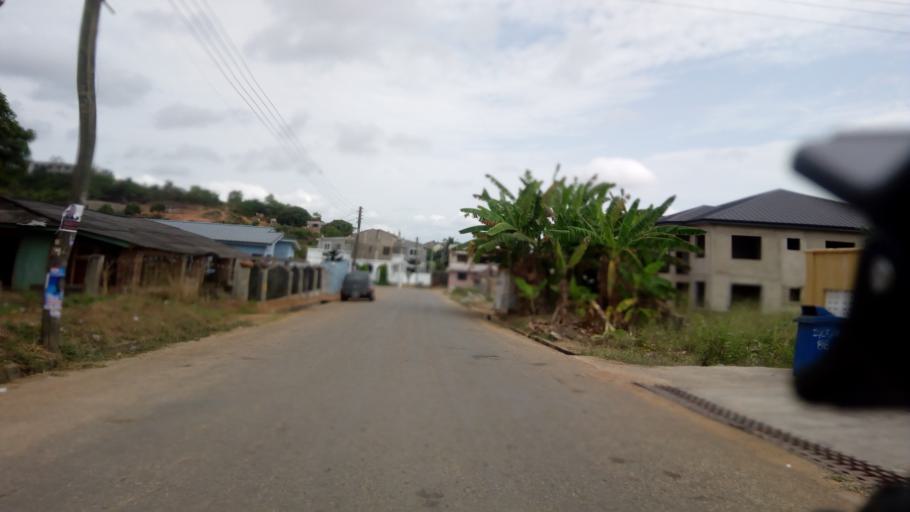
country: GH
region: Central
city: Cape Coast
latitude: 5.1068
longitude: -1.2713
